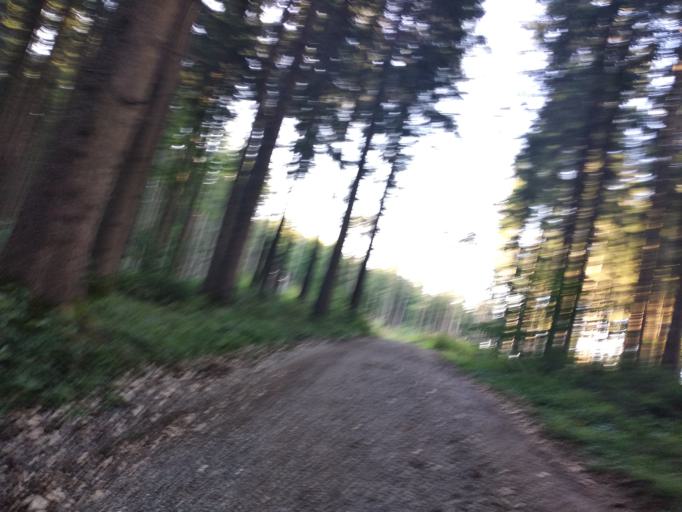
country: DE
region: Bavaria
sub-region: Swabia
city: Lautrach
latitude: 47.8845
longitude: 10.1031
